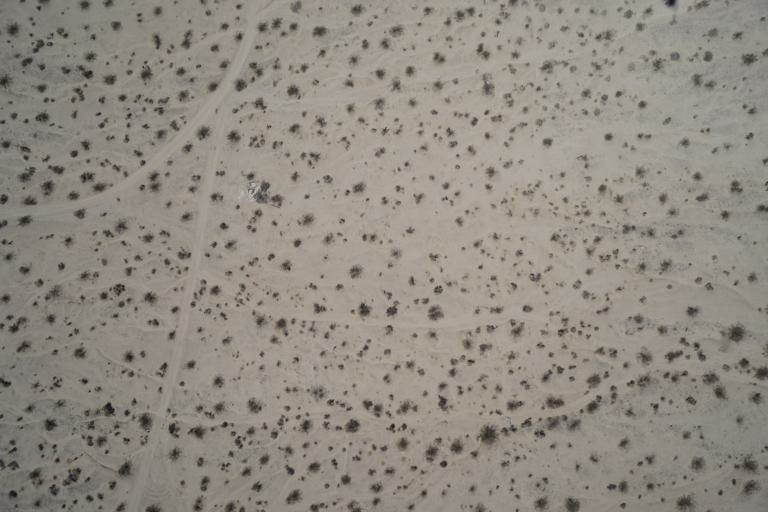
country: US
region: California
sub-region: San Bernardino County
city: Twentynine Palms
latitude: 34.1271
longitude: -116.0265
